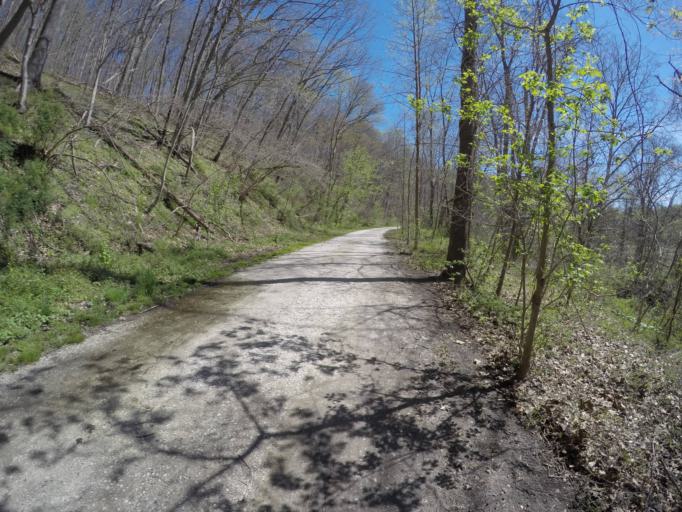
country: US
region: Maryland
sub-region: Baltimore County
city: Hunt Valley
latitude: 39.5857
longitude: -76.6112
